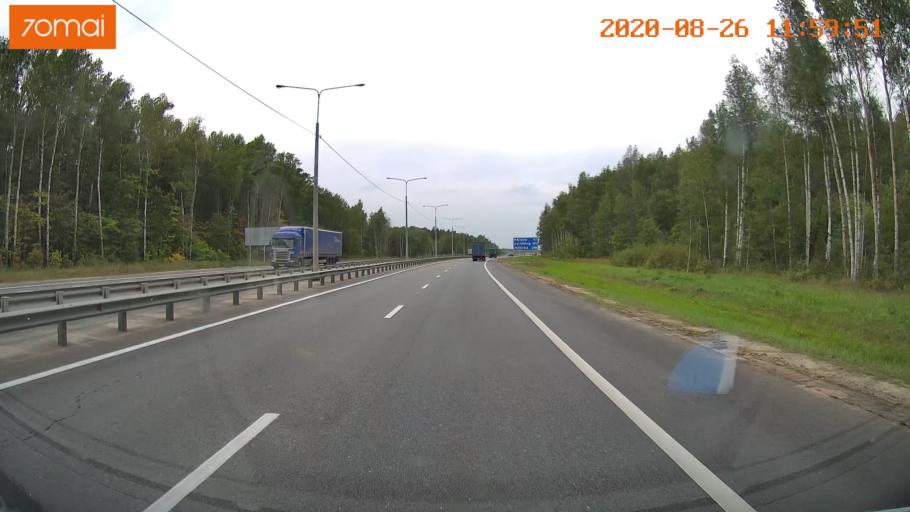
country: RU
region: Rjazan
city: Kiritsy
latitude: 54.2861
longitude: 40.2882
